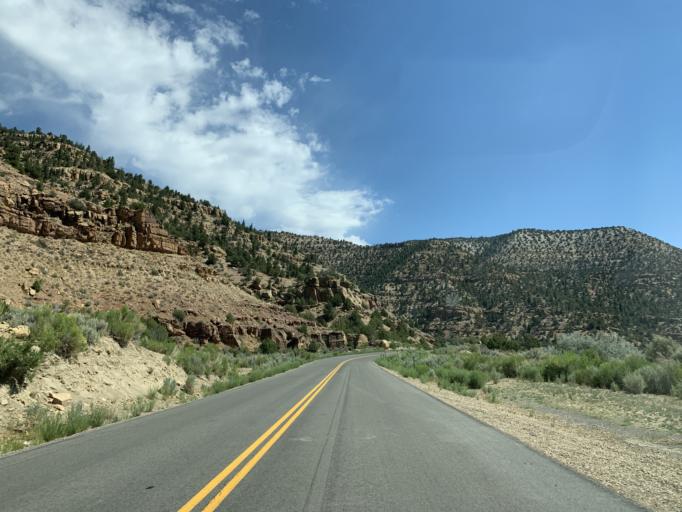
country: US
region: Utah
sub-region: Carbon County
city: East Carbon City
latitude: 39.7837
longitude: -110.4198
